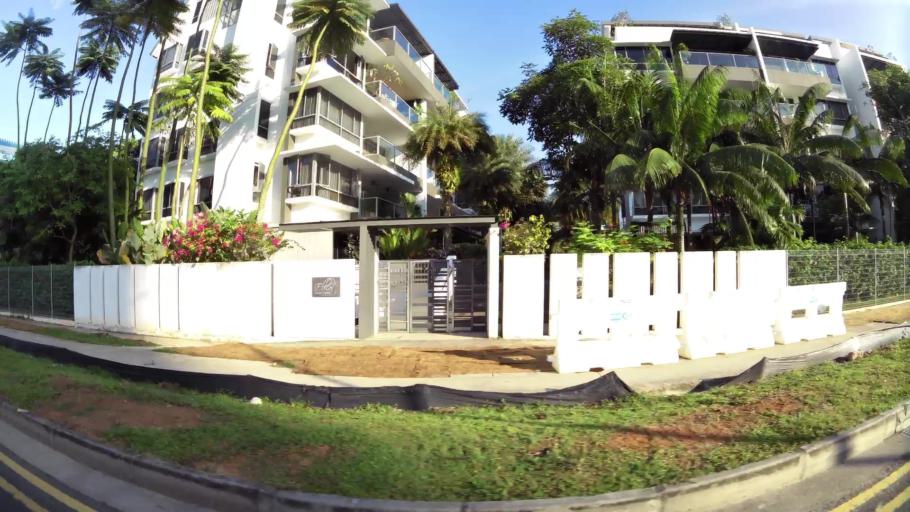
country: SG
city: Singapore
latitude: 1.3103
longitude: 103.9309
